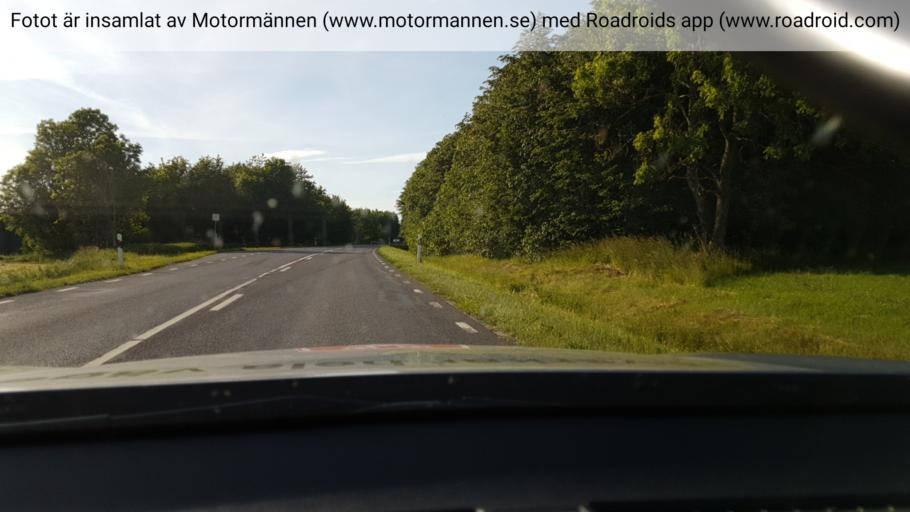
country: SE
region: Vaestra Goetaland
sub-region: Falkopings Kommun
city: Falkoeping
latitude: 58.0656
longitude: 13.5296
